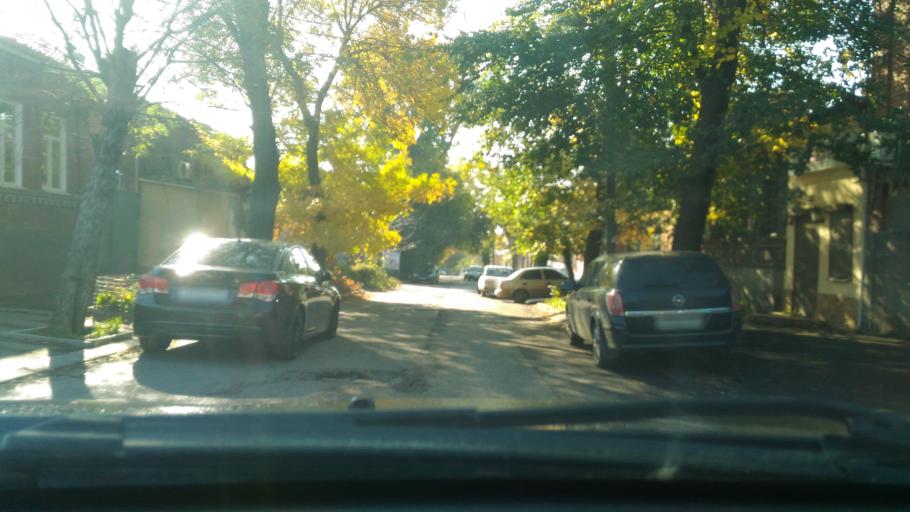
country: RU
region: Rostov
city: Rostov-na-Donu
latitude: 47.2275
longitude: 39.7688
